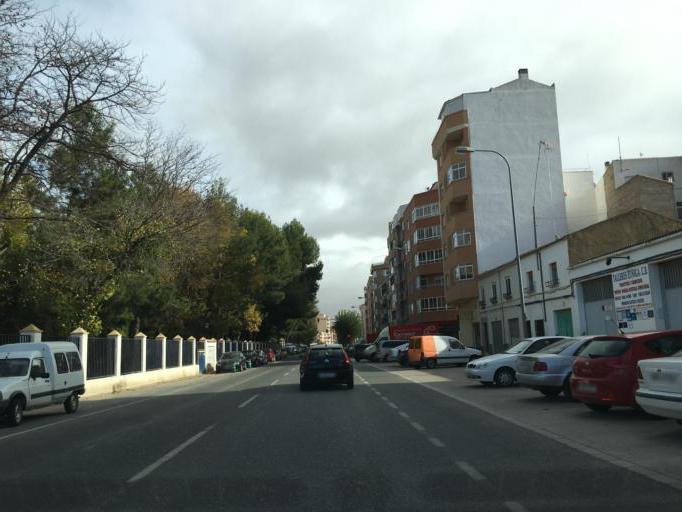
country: ES
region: Castille-La Mancha
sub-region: Provincia de Albacete
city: Albacete
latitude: 38.9983
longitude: -1.8758
